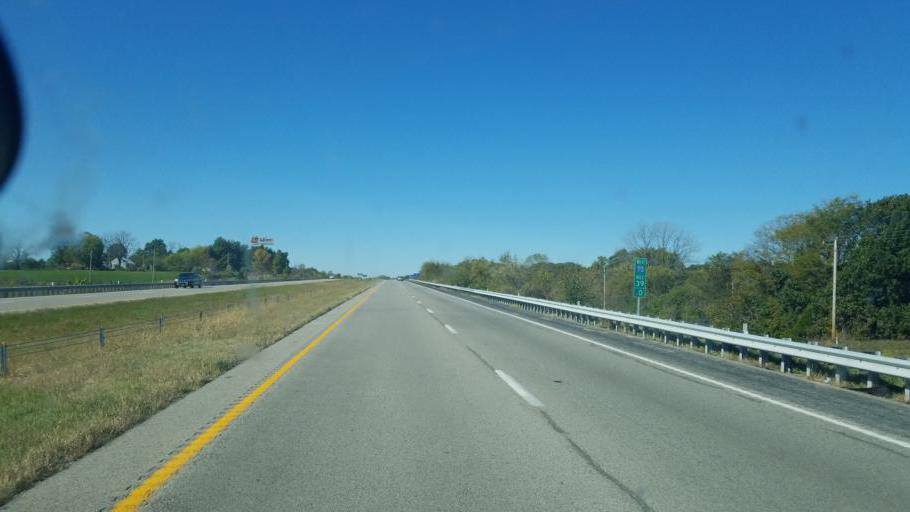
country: US
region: Missouri
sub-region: Lafayette County
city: Odessa
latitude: 39.0071
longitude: -93.9230
